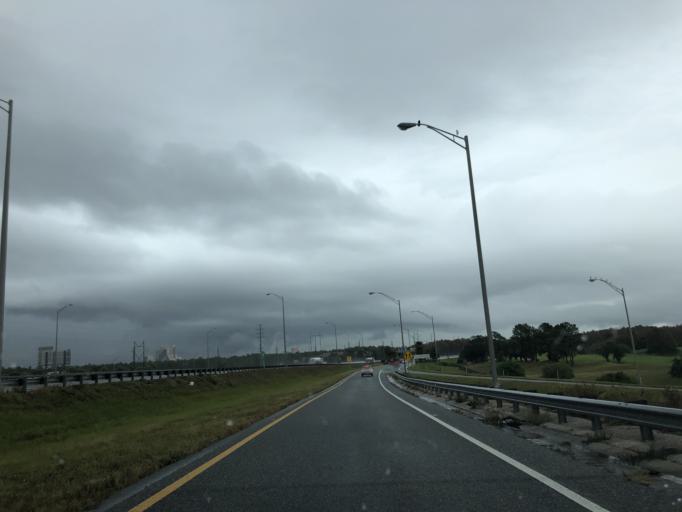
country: US
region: Florida
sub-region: Osceola County
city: Celebration
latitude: 28.3419
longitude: -81.5167
